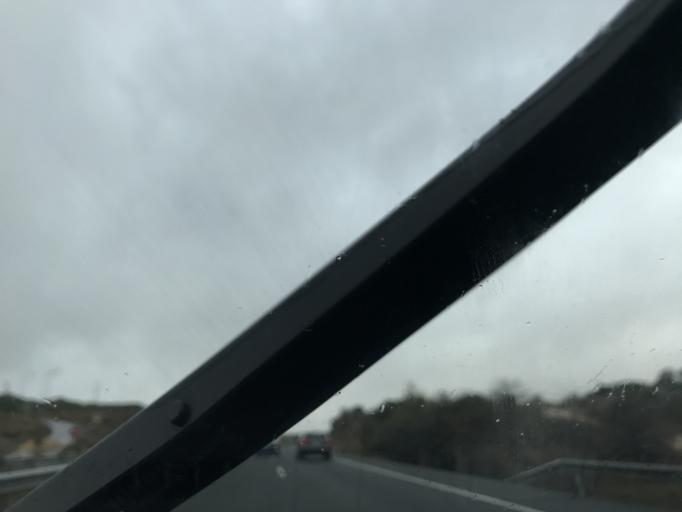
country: ES
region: Andalusia
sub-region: Provincia de Malaga
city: Mollina
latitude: 37.1059
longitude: -4.6527
